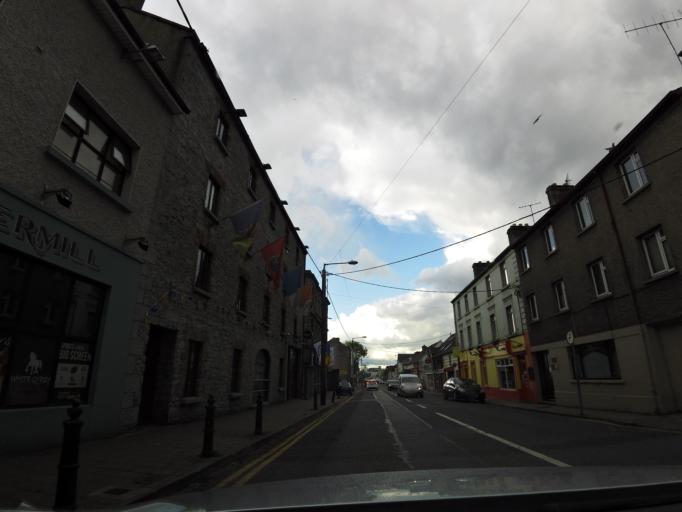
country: IE
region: Munster
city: Thurles
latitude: 52.6786
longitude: -7.8133
